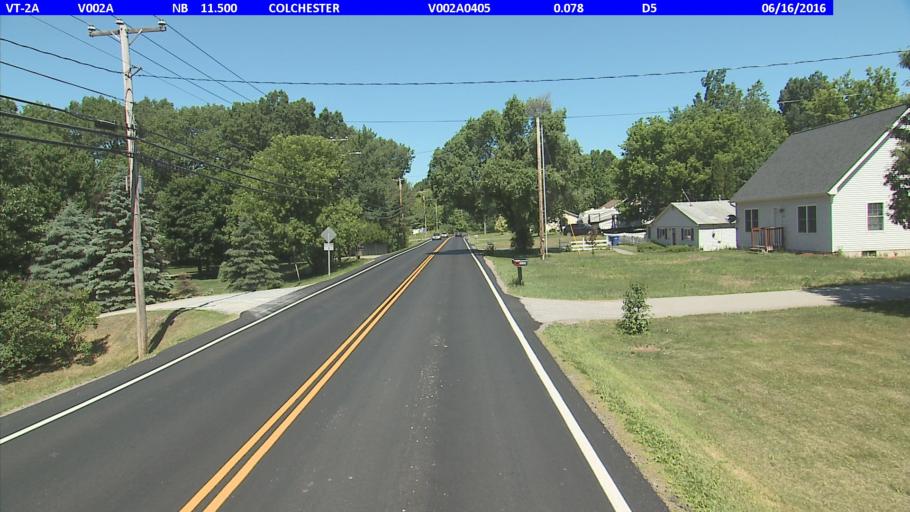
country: US
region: Vermont
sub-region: Chittenden County
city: Colchester
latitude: 44.5292
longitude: -73.1302
